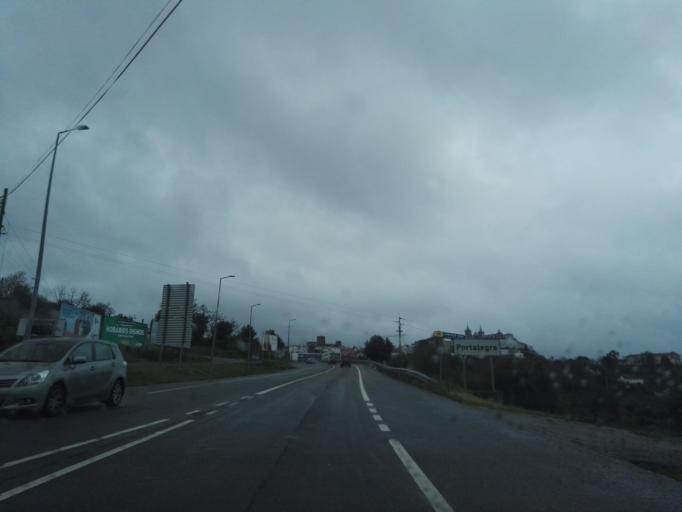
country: PT
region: Portalegre
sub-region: Portalegre
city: Portalegre
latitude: 39.2978
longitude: -7.4365
